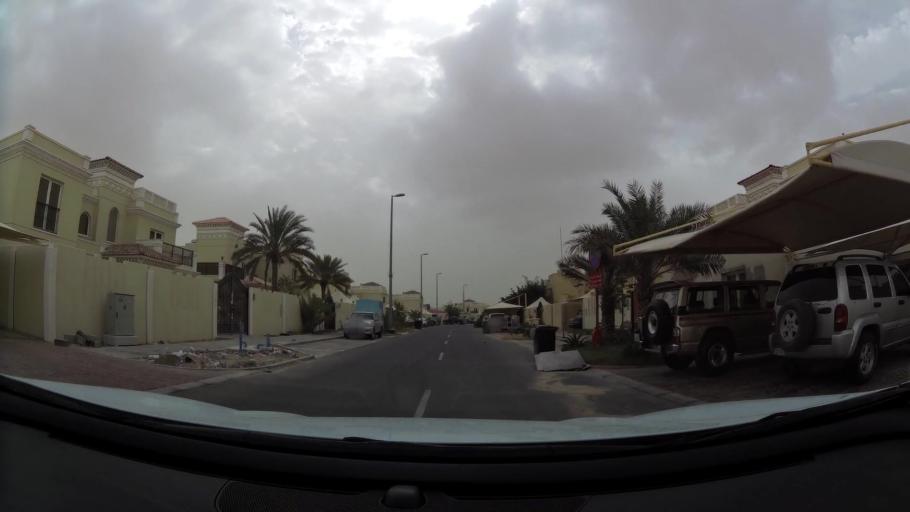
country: AE
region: Abu Dhabi
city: Abu Dhabi
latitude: 24.4487
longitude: 54.7156
